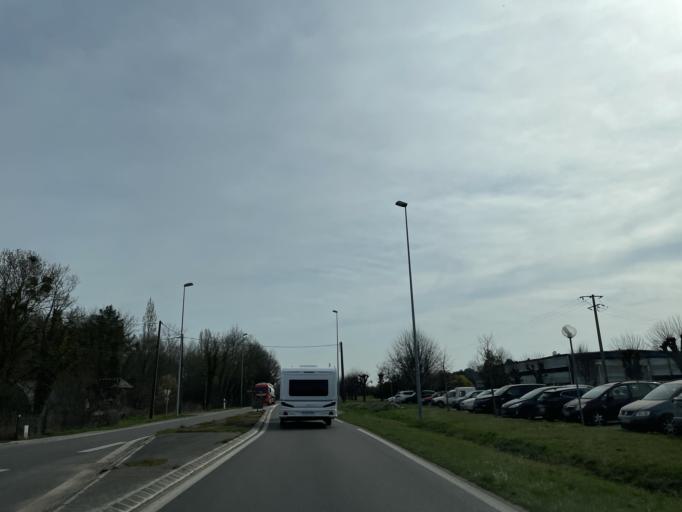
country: FR
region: Champagne-Ardenne
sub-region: Departement de l'Aube
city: Romilly-sur-Seine
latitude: 48.5144
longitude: 3.6664
